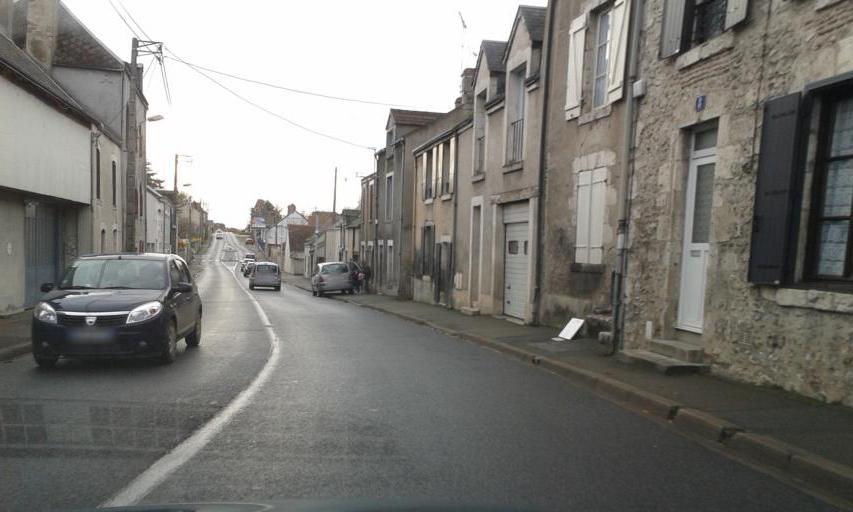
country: FR
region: Centre
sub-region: Departement du Loiret
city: Meung-sur-Loire
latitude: 47.8280
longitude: 1.6924
